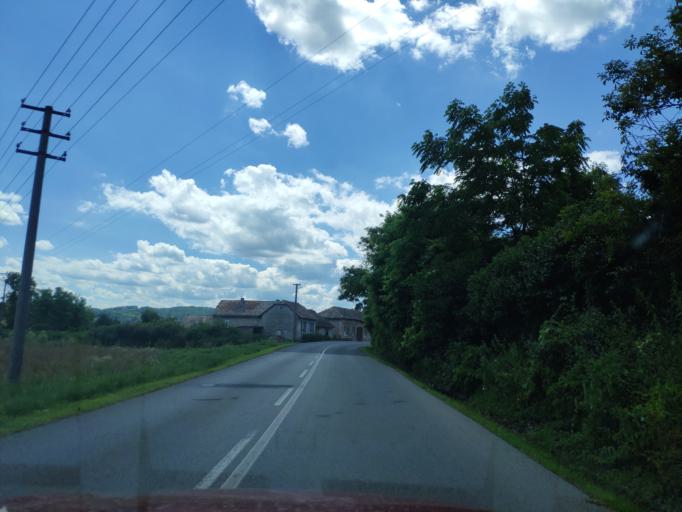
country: HU
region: Borsod-Abauj-Zemplen
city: Ozd
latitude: 48.3050
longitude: 20.2458
